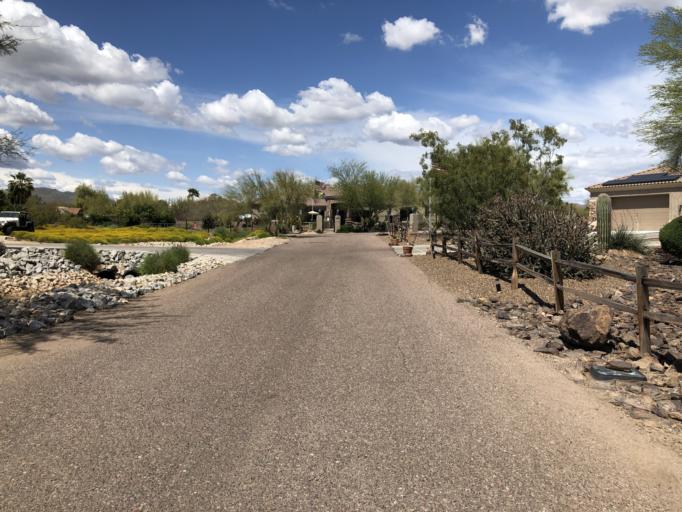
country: US
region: Arizona
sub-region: Maricopa County
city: Anthem
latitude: 33.8362
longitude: -112.0725
